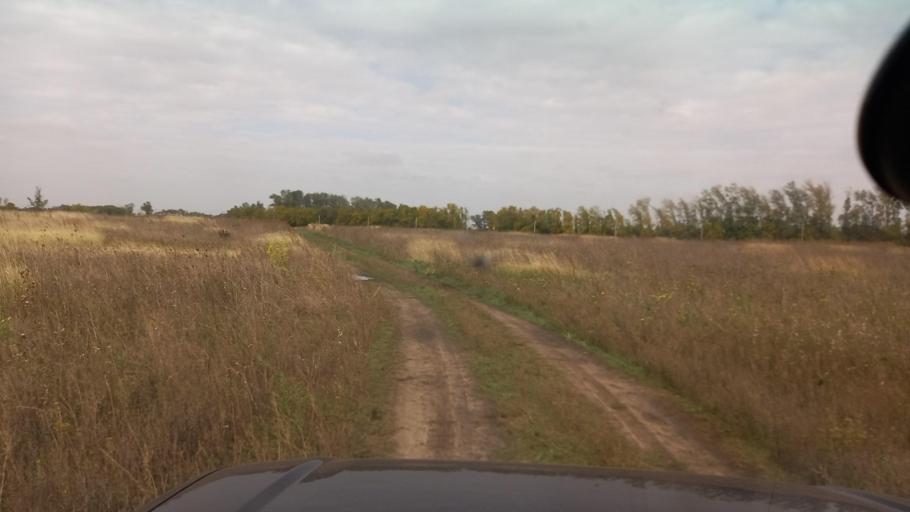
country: RU
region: Krasnodarskiy
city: Krasnodar
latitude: 45.1279
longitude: 38.9196
